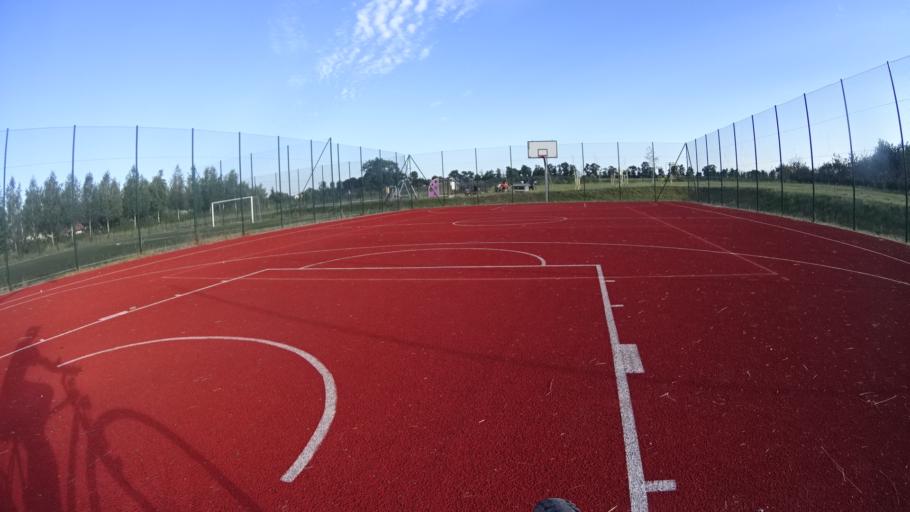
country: PL
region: Masovian Voivodeship
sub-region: Powiat grojecki
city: Goszczyn
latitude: 51.6926
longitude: 20.8148
